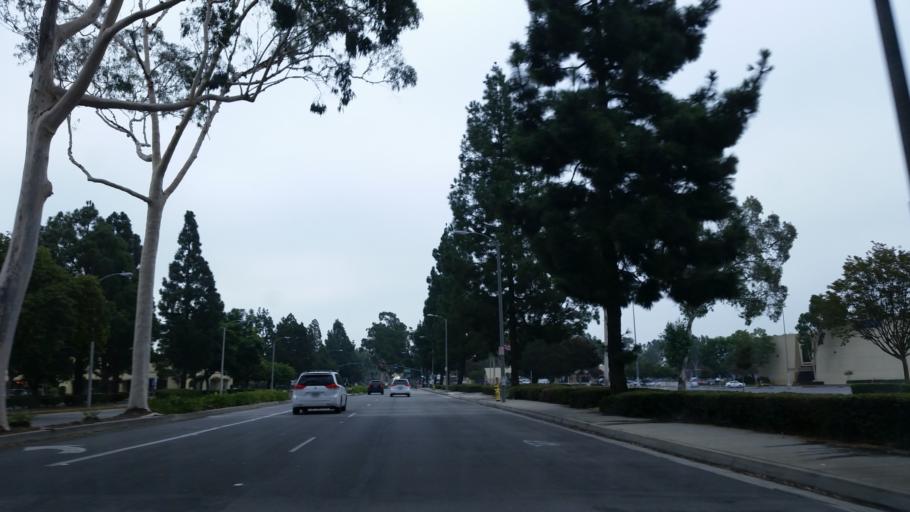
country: US
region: California
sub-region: Los Angeles County
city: Artesia
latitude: 33.8656
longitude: -118.0971
